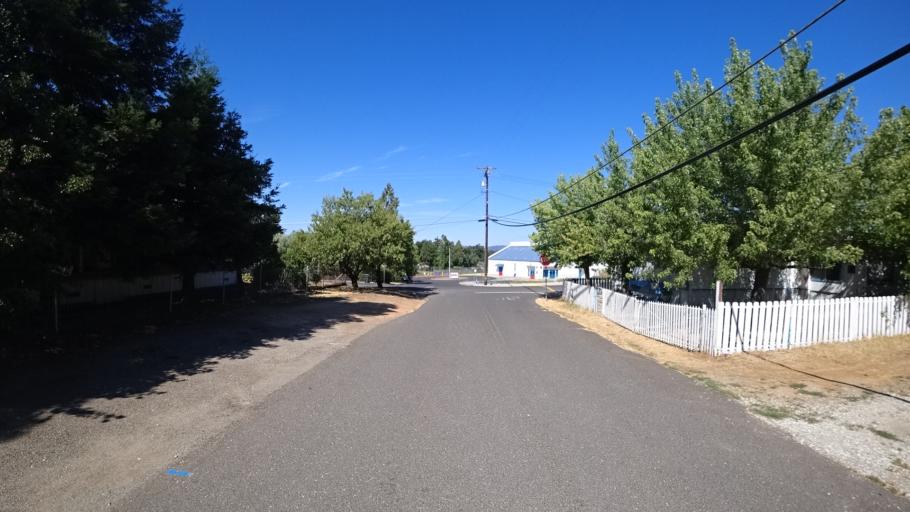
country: US
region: California
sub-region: Calaveras County
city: Angels Camp
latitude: 38.0742
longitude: -120.5494
